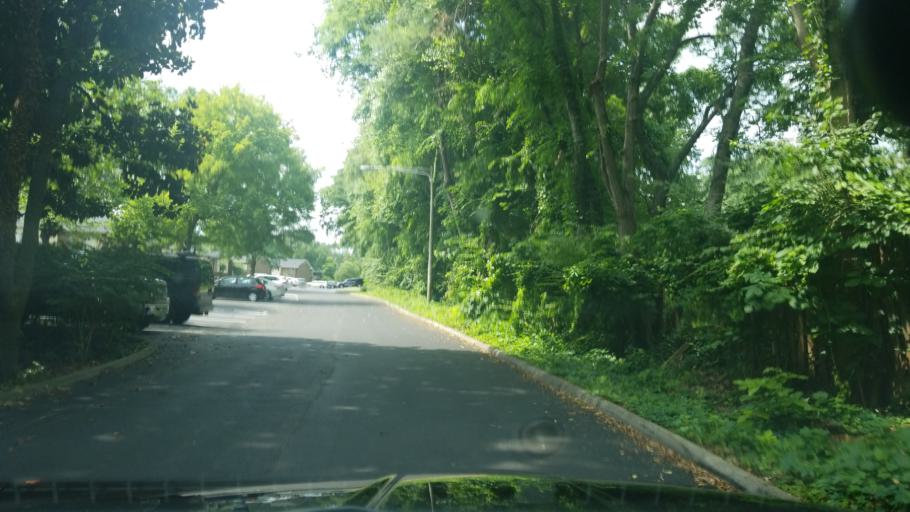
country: US
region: Tennessee
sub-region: Davidson County
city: Oak Hill
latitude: 36.0840
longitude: -86.7388
